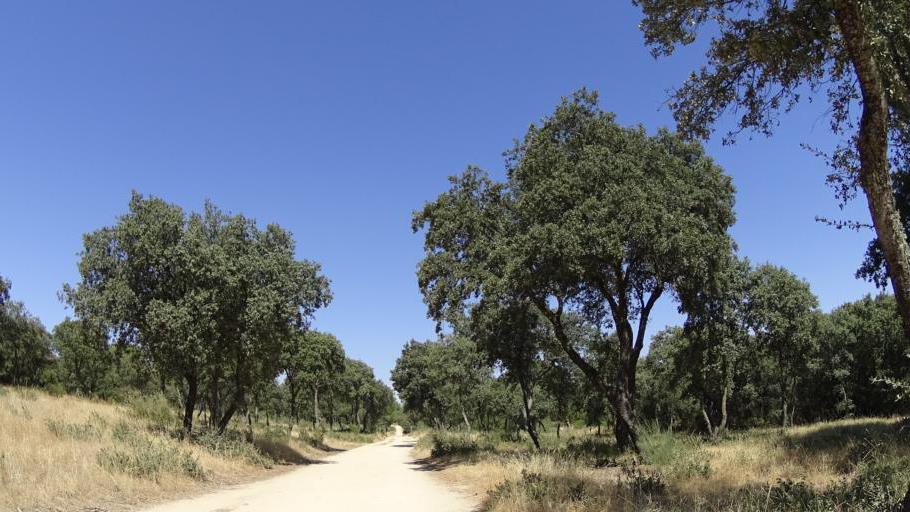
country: ES
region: Madrid
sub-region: Provincia de Madrid
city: Majadahonda
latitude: 40.4402
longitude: -3.8631
